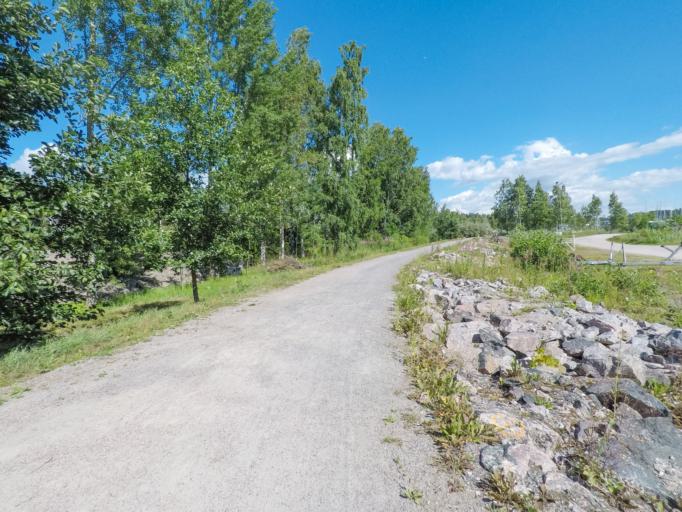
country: FI
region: Uusimaa
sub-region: Helsinki
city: Vantaa
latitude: 60.2046
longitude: 25.0957
